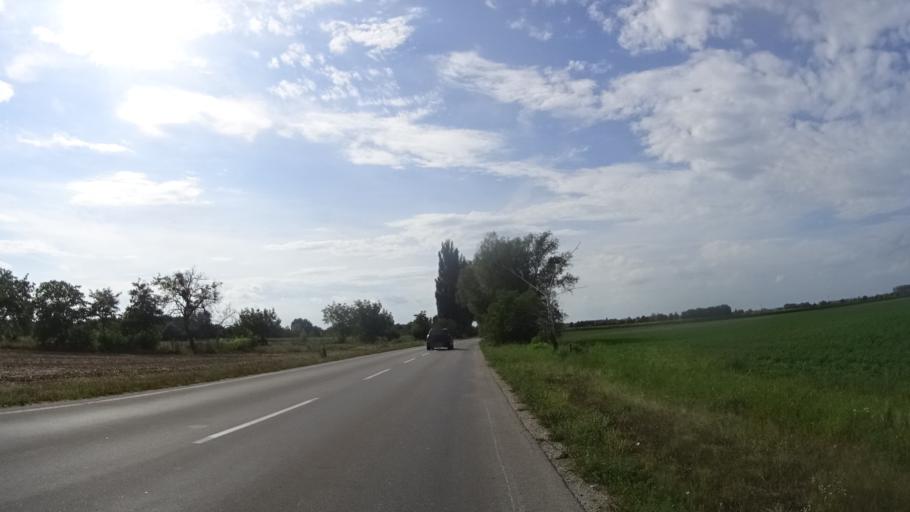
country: SK
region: Trnavsky
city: Gabcikovo
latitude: 47.9139
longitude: 17.5112
